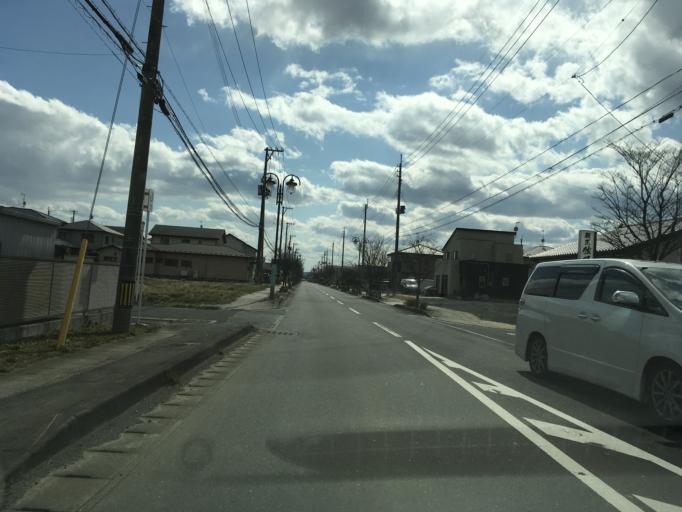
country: JP
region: Miyagi
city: Wakuya
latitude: 38.7063
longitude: 141.2154
